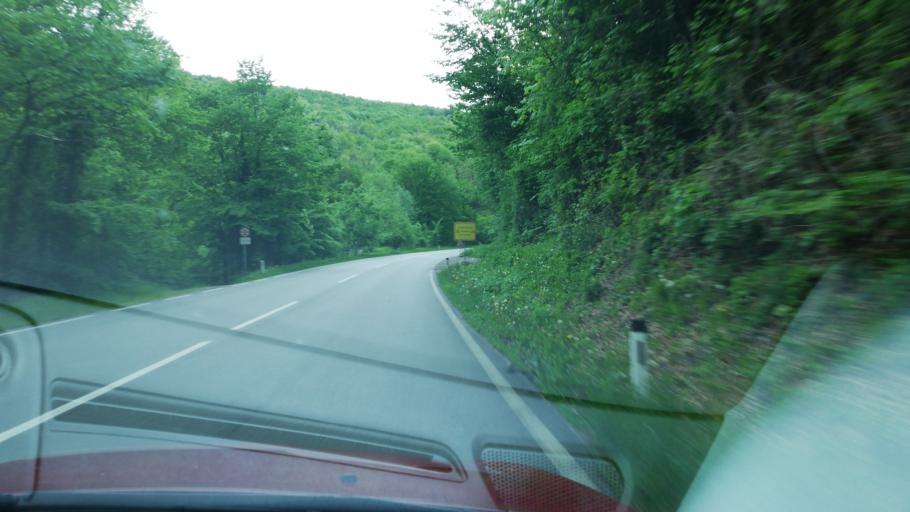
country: AT
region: Lower Austria
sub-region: Politischer Bezirk Modling
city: Gaaden
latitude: 48.0132
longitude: 16.1629
